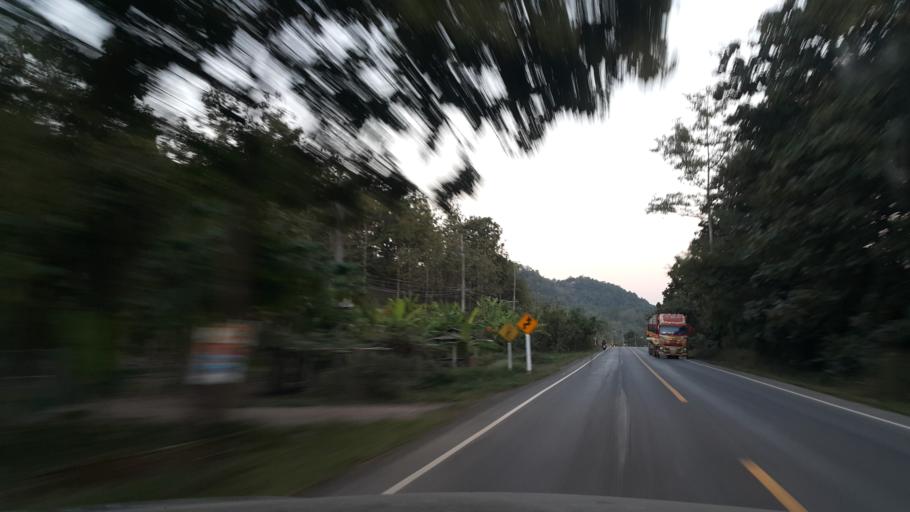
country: TH
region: Phrae
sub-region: Amphoe Wang Chin
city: Wang Chin
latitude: 17.9720
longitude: 99.6215
